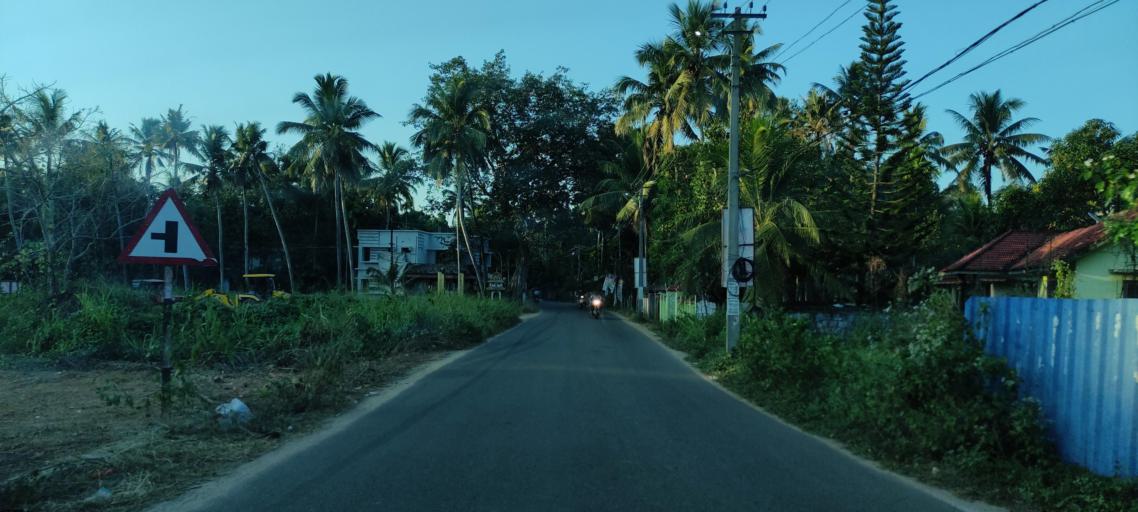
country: IN
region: Kerala
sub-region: Alappuzha
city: Kayankulam
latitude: 9.1923
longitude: 76.4681
